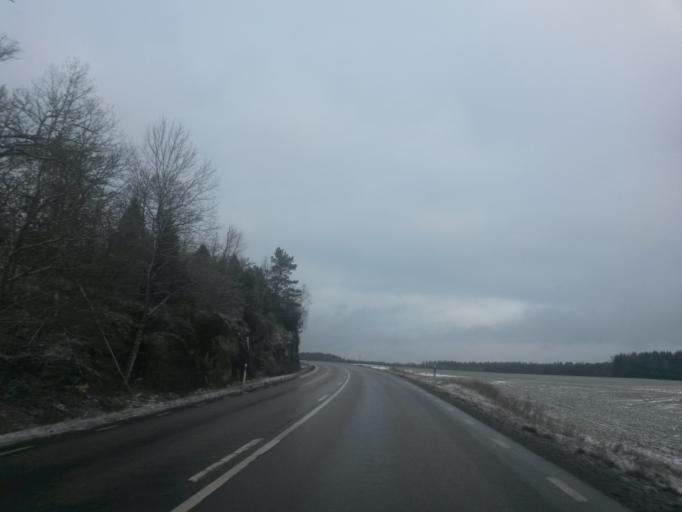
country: SE
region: Vaestra Goetaland
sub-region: Vargarda Kommun
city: Jonstorp
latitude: 58.0928
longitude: 12.6594
